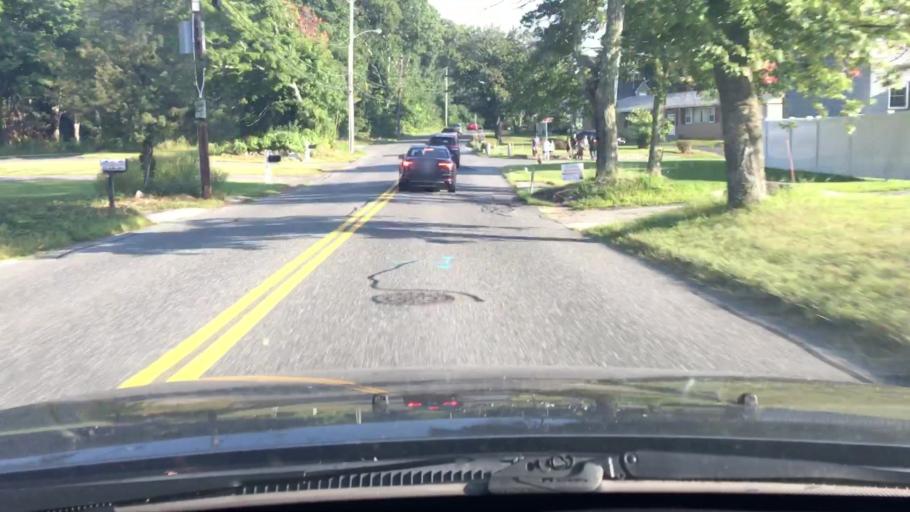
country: US
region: Massachusetts
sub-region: Middlesex County
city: Hopkinton
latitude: 42.1847
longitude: -71.5393
